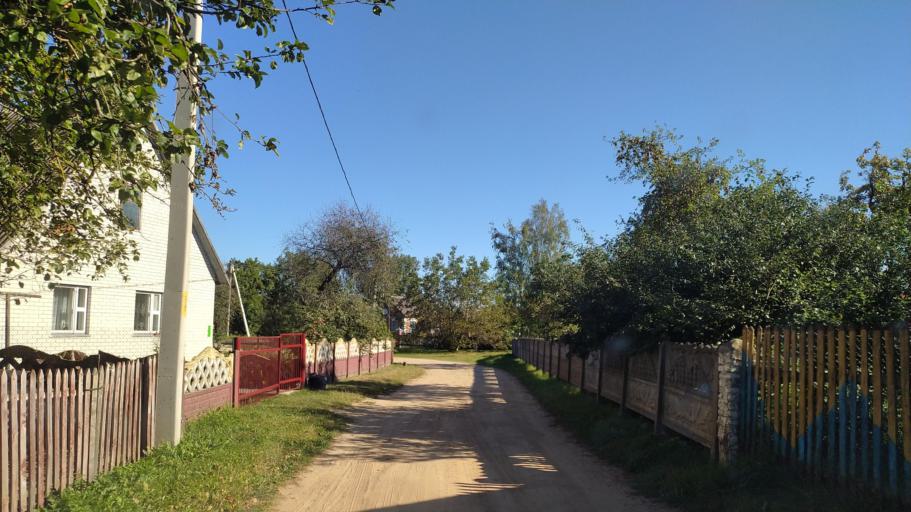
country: BY
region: Brest
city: Pruzhany
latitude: 52.4847
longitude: 24.7094
